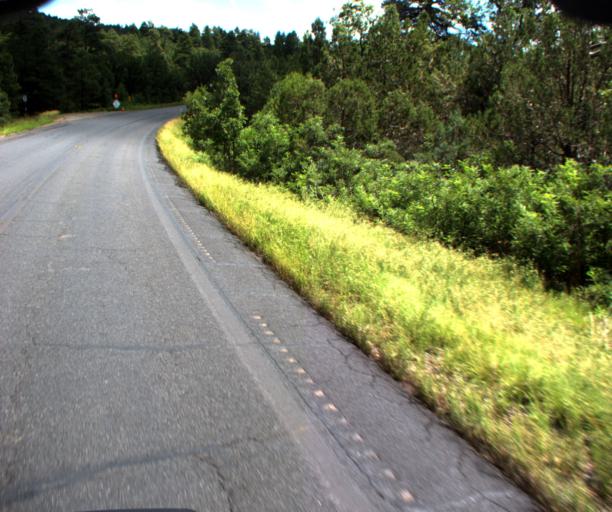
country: US
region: Arizona
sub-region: Gila County
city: Pine
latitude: 34.5214
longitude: -111.5099
